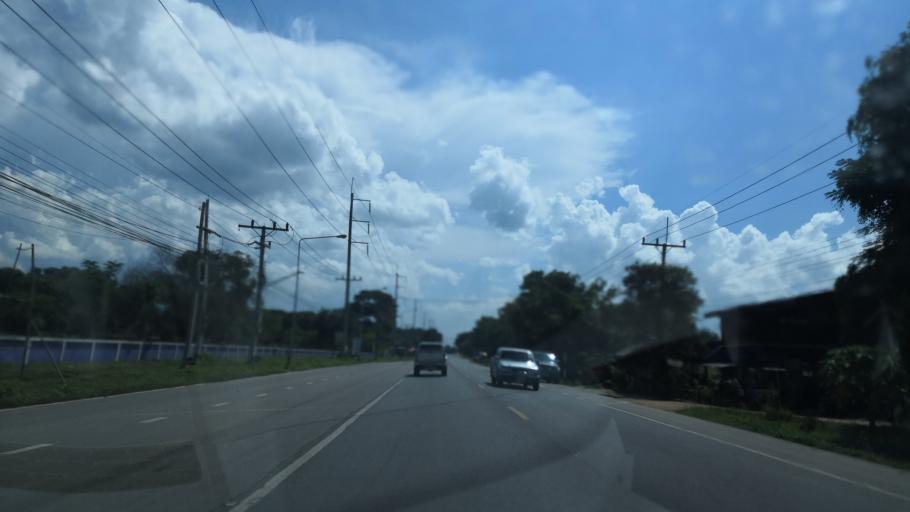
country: TH
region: Chiang Rai
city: Mae Suai
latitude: 19.6074
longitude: 99.5091
